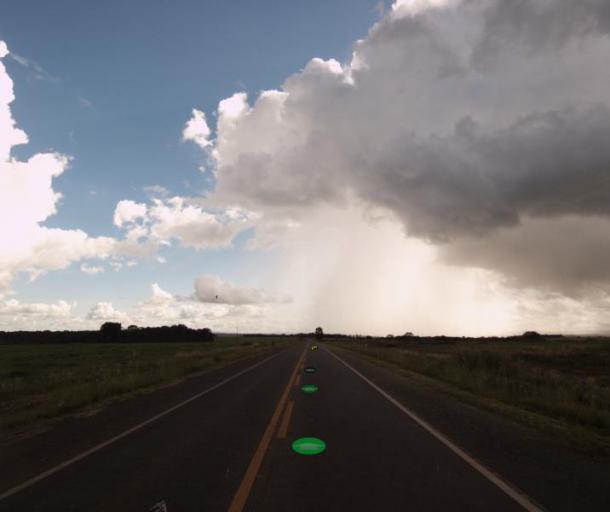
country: BR
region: Goias
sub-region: Itaberai
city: Itaberai
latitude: -15.9905
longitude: -49.7233
